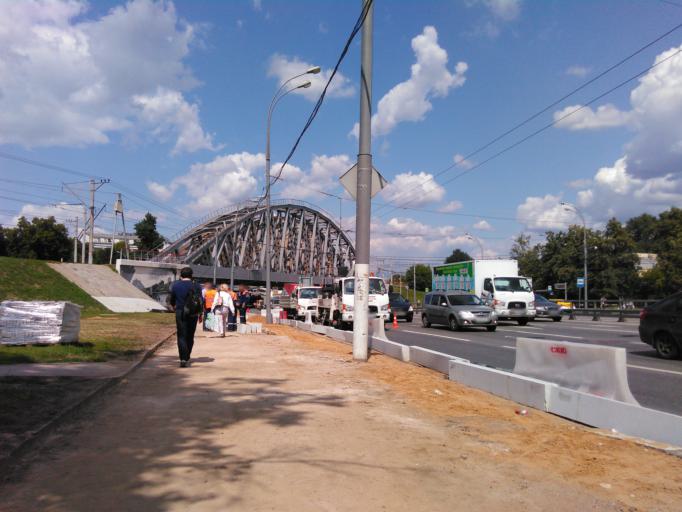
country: RU
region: Moscow
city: Zamoskvorech'ye
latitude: 55.7018
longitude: 37.6211
